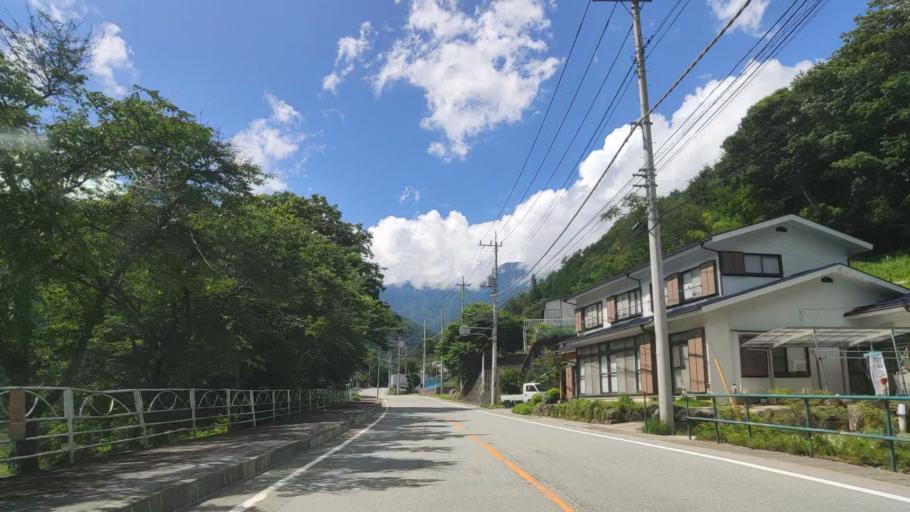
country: JP
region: Yamanashi
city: Enzan
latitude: 35.8471
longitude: 138.7617
